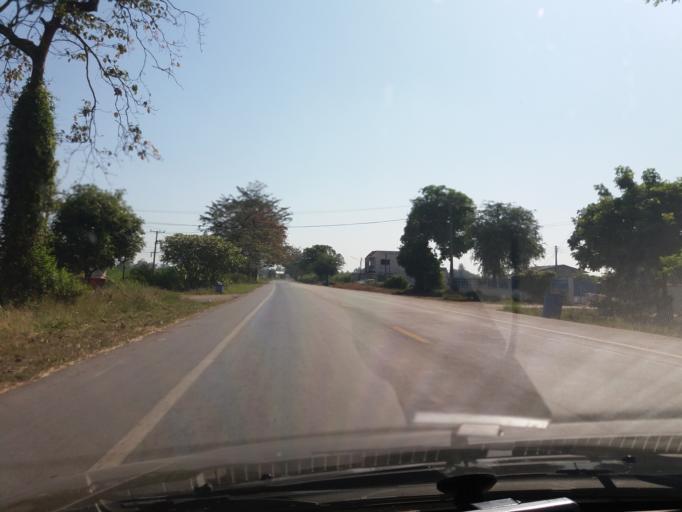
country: TH
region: Kamphaeng Phet
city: Khlong Khlung
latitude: 16.2071
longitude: 99.7529
